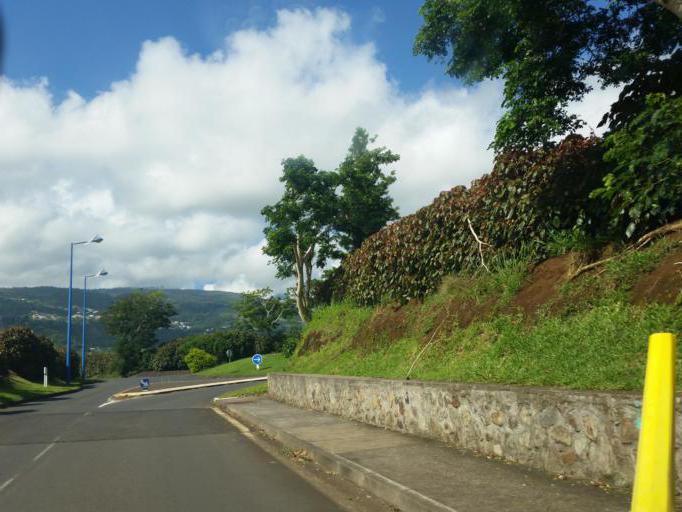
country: RE
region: Reunion
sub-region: Reunion
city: Sainte-Marie
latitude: -20.9243
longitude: 55.5305
